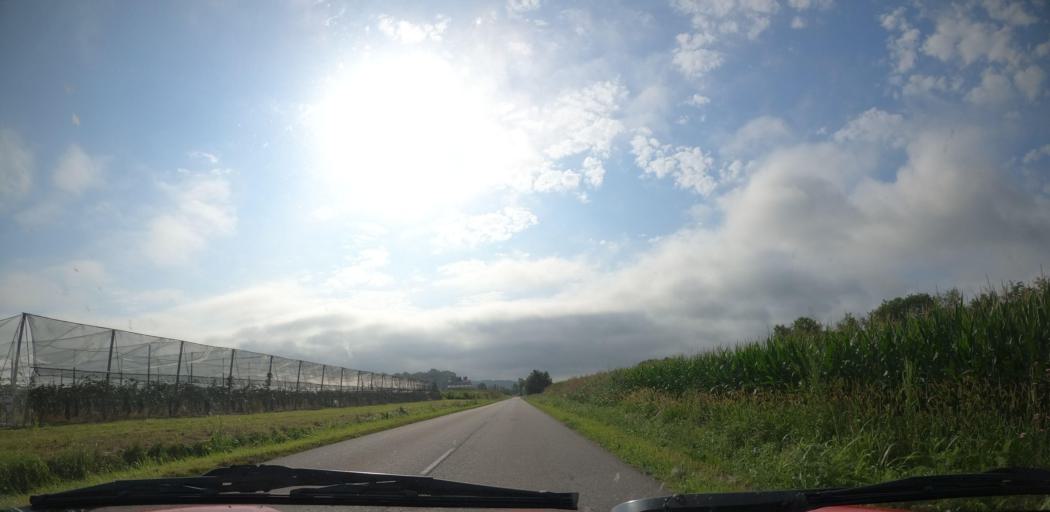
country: FR
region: Aquitaine
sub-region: Departement des Landes
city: Peyrehorade
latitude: 43.5366
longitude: -1.0747
